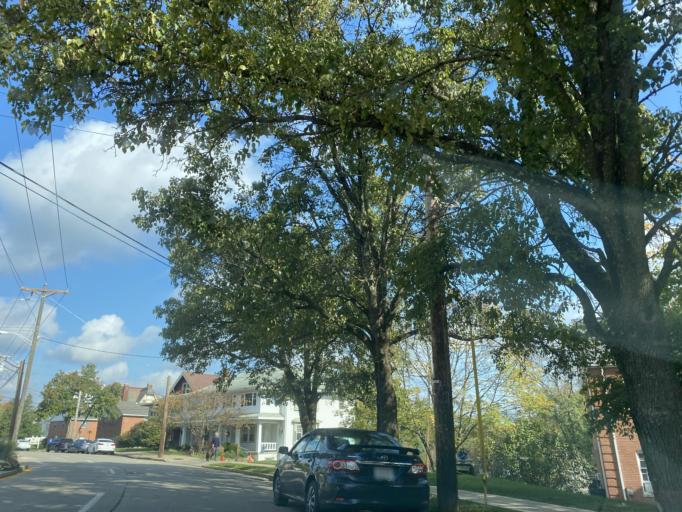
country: US
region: Kentucky
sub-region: Campbell County
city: Fort Thomas
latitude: 39.0761
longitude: -84.4471
